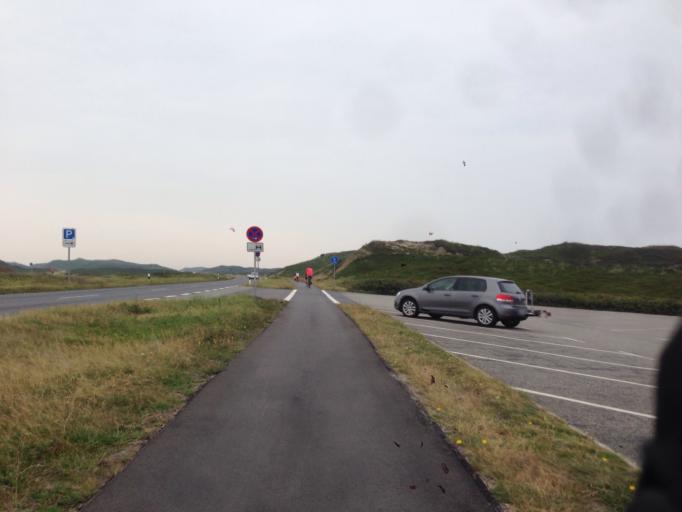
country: DE
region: Schleswig-Holstein
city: Westerland
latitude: 54.8107
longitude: 8.2887
